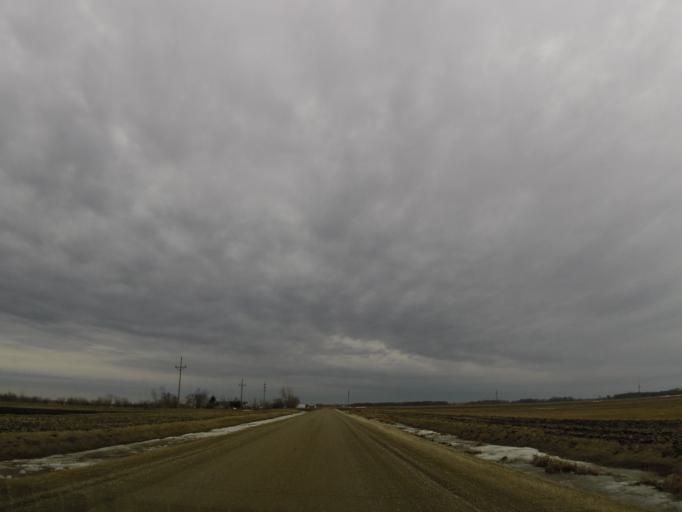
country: US
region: North Dakota
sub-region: Walsh County
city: Grafton
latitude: 48.4198
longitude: -97.4448
